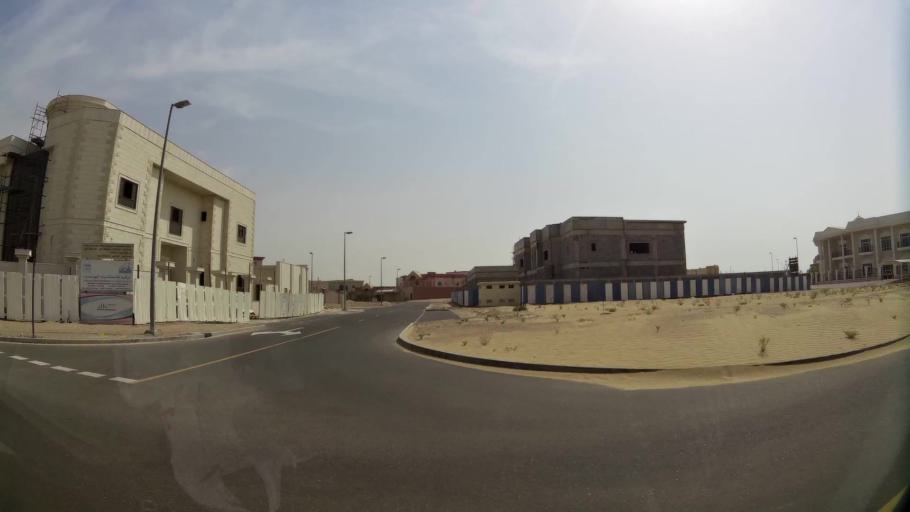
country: AE
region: Ash Shariqah
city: Sharjah
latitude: 25.2593
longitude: 55.4665
